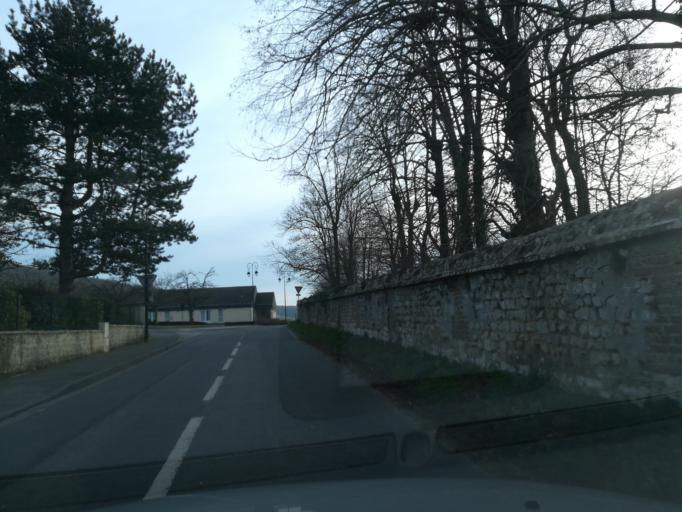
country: FR
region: Haute-Normandie
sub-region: Departement de la Seine-Maritime
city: Saint-Martin-de-Boscherville
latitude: 49.4407
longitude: 0.9632
